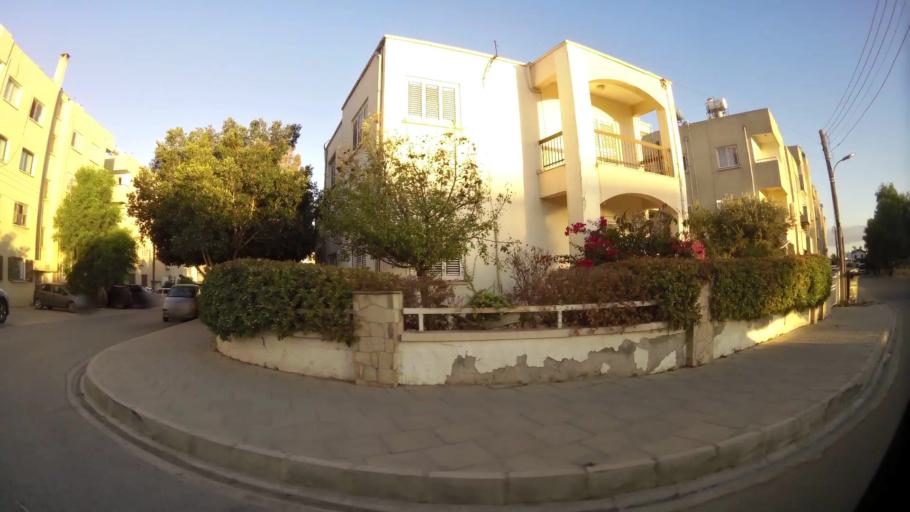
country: CY
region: Lefkosia
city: Nicosia
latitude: 35.2052
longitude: 33.3266
